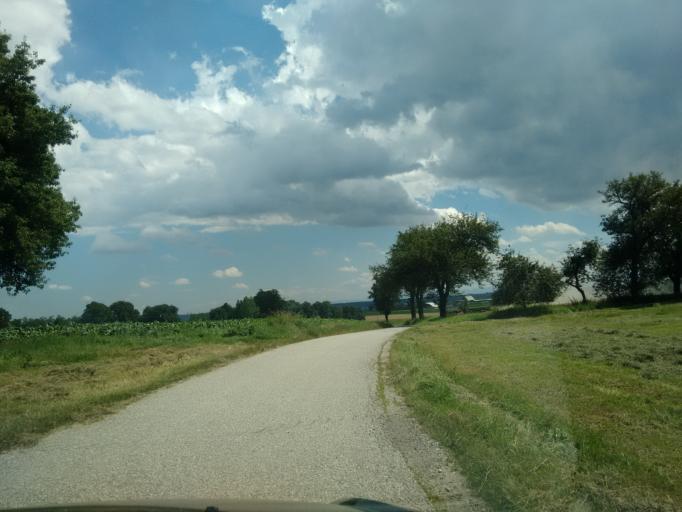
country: AT
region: Upper Austria
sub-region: Wels-Land
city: Gunskirchen
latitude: 48.1769
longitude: 13.9568
